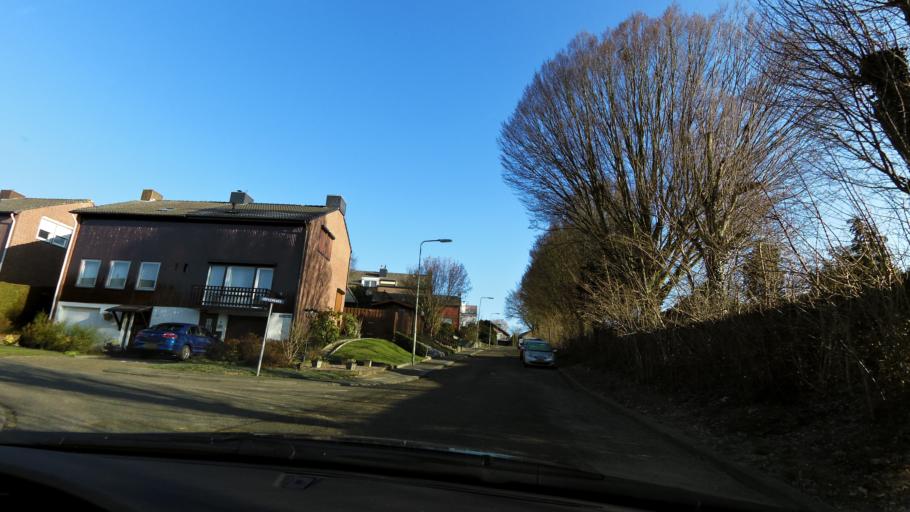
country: NL
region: Limburg
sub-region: Gemeente Simpelveld
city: Simpelveld
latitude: 50.8094
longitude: 5.9573
